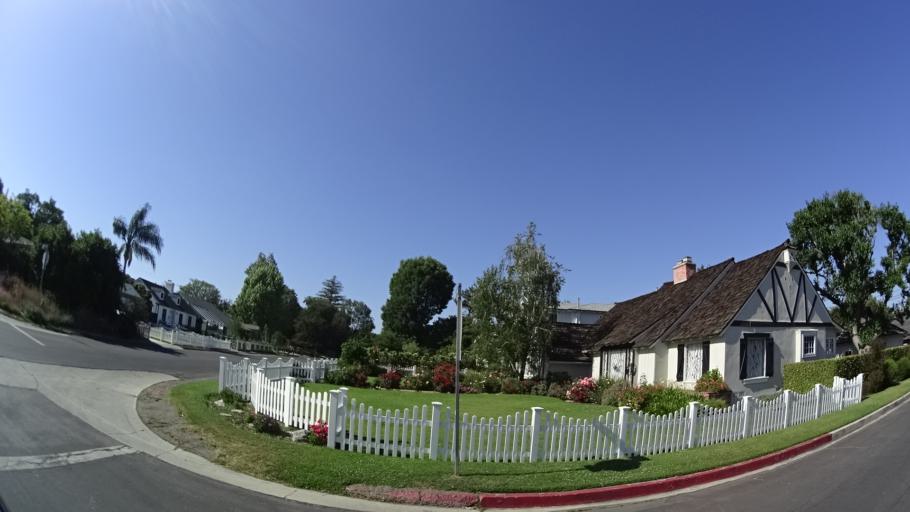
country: US
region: California
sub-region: Los Angeles County
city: North Hollywood
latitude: 34.1522
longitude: -118.3920
